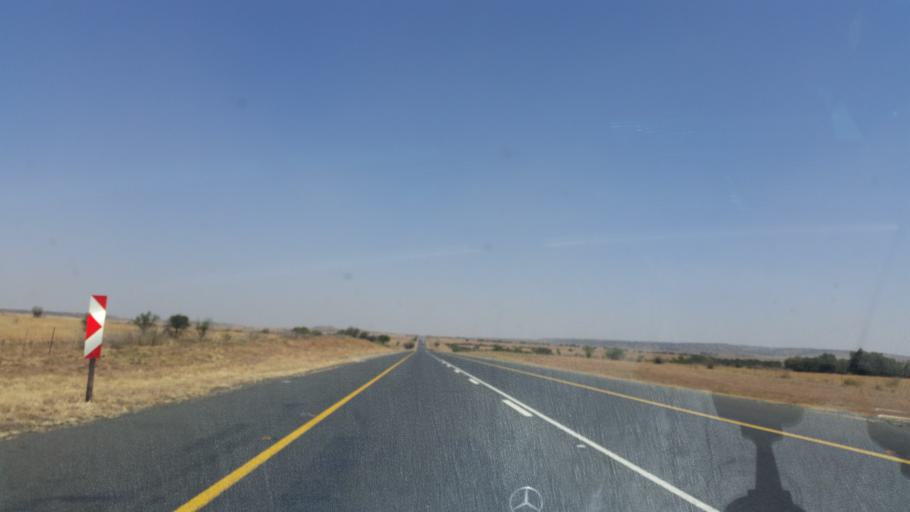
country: ZA
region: Orange Free State
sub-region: Lejweleputswa District Municipality
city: Winburg
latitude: -28.6701
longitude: 26.8461
